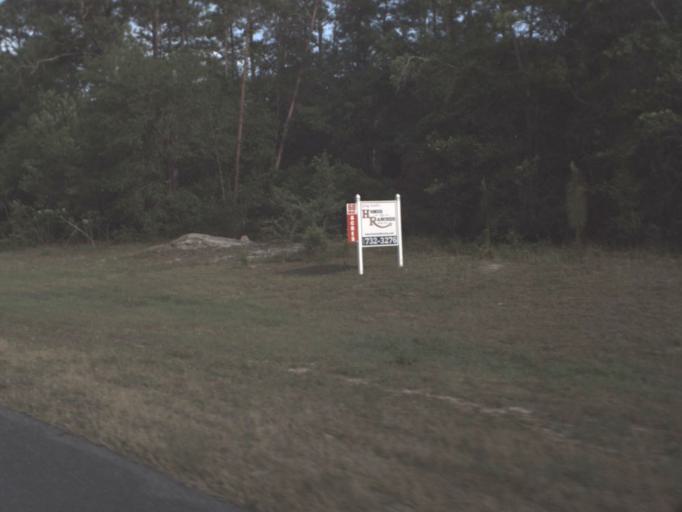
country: US
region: Florida
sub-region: Marion County
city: Silver Springs Shores
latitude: 29.1719
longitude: -81.8559
